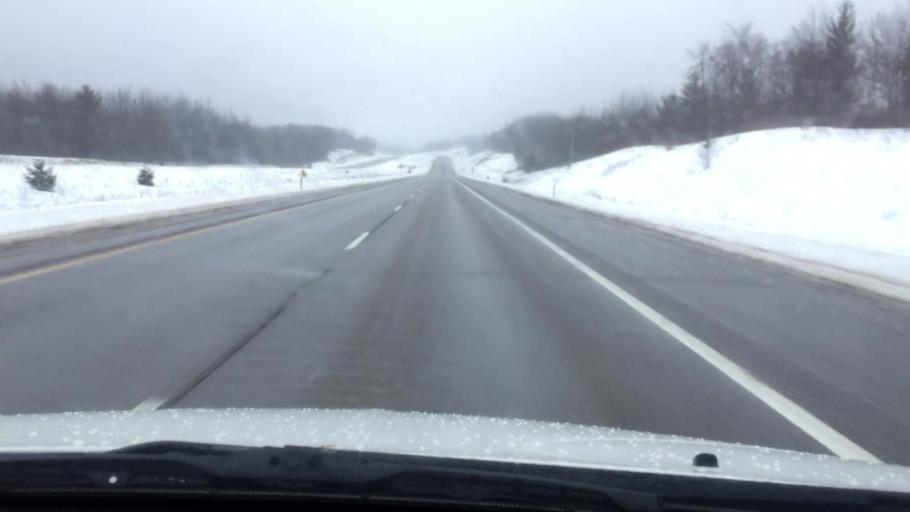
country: US
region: Michigan
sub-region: Wexford County
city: Manton
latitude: 44.3441
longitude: -85.4054
